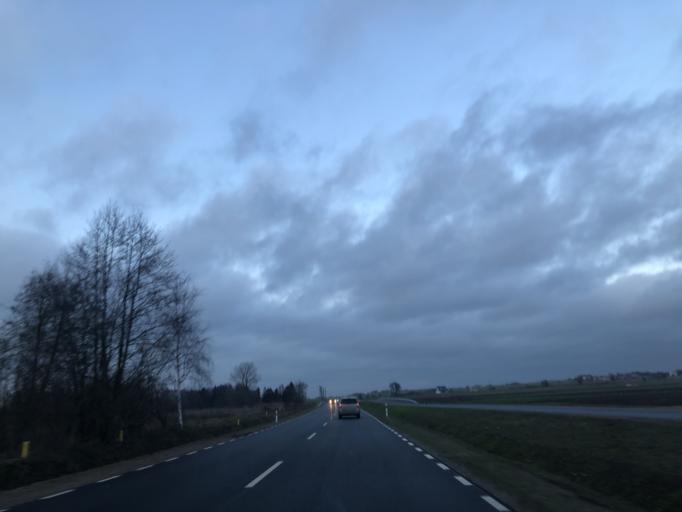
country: PL
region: Podlasie
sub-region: Lomza
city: Lomza
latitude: 53.1321
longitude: 22.0494
